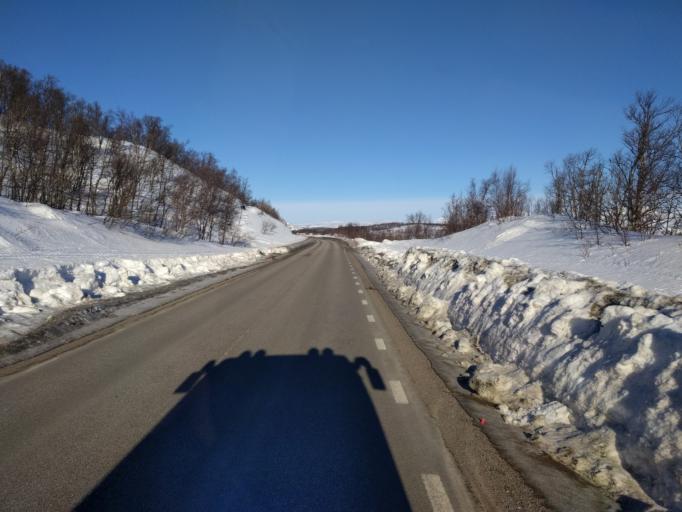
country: NO
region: Troms
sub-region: Bardu
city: Setermoen
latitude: 68.4327
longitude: 18.6651
